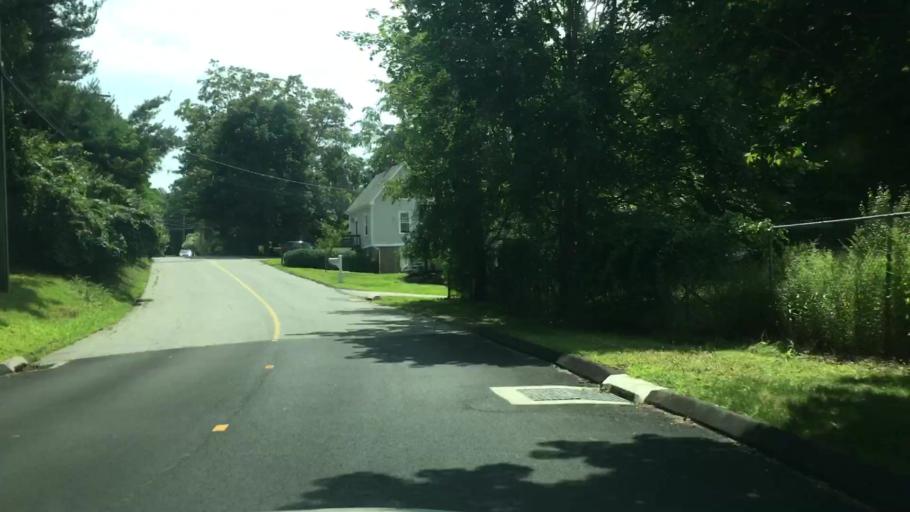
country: US
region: Connecticut
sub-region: Middlesex County
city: Deep River Center
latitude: 41.3453
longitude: -72.4469
